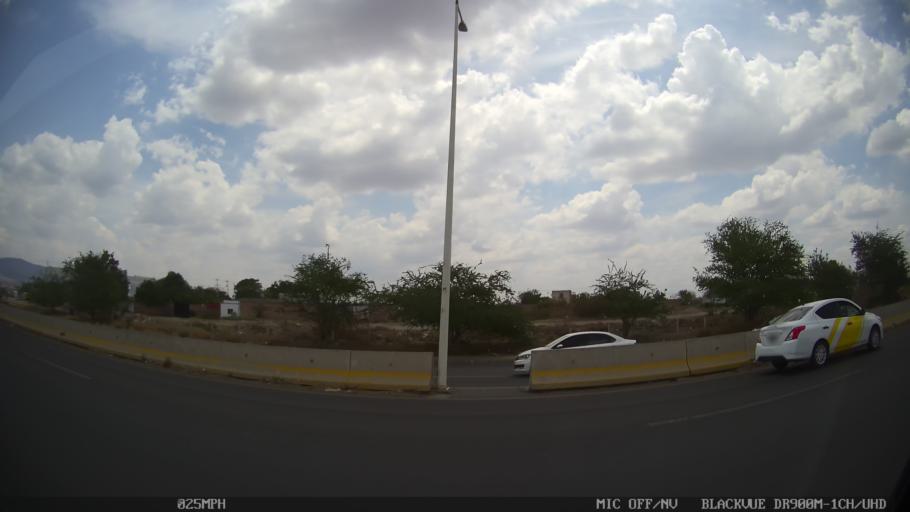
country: MX
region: Jalisco
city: Tonala
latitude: 20.6783
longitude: -103.2340
